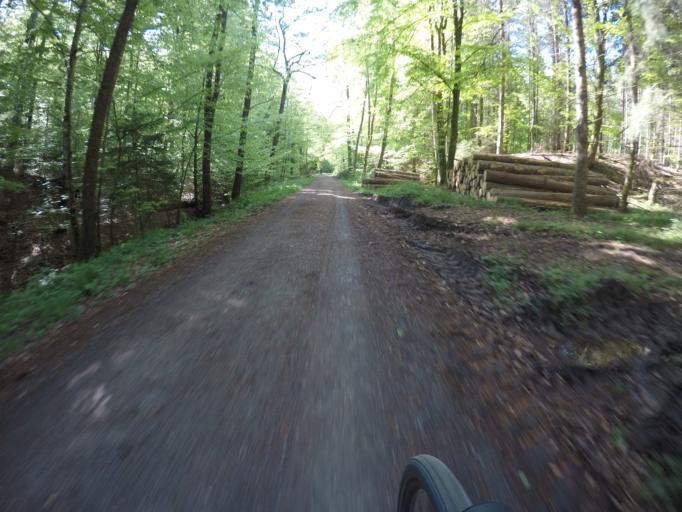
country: DE
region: Baden-Wuerttemberg
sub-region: Tuebingen Region
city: Dettenhausen
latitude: 48.5824
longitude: 9.0940
